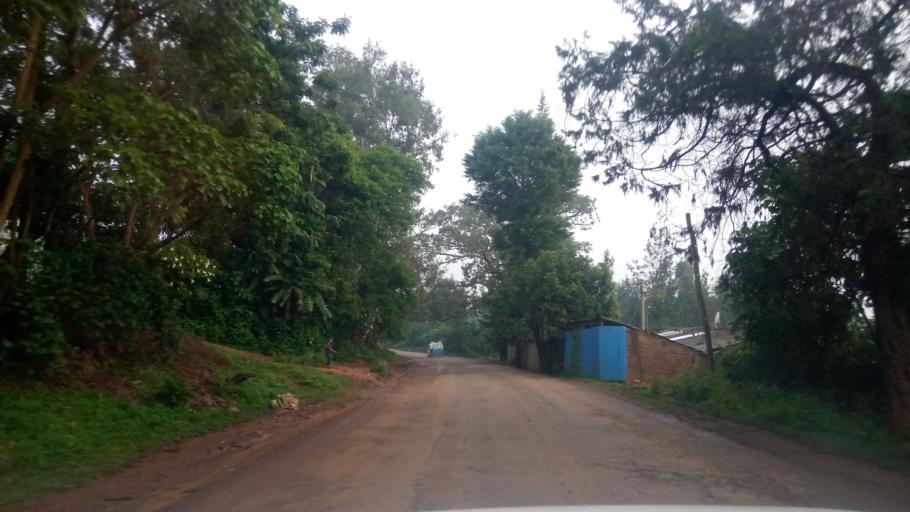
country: ET
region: Oromiya
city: Jima
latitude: 7.6918
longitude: 36.8243
